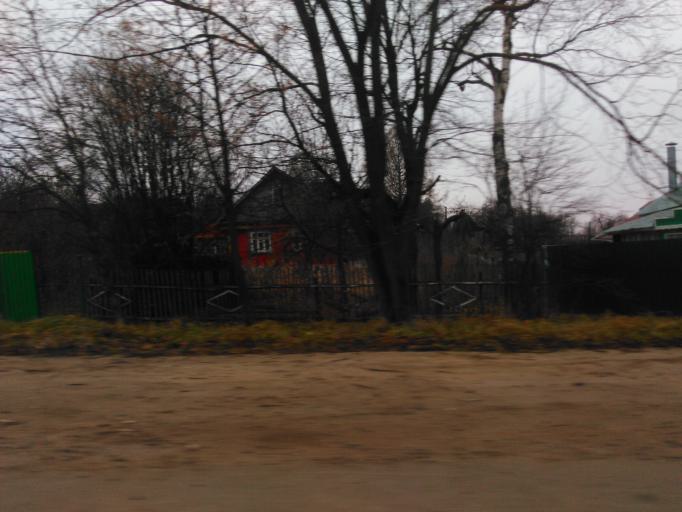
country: RU
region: Moskovskaya
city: Sofrino
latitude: 56.1227
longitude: 37.9669
